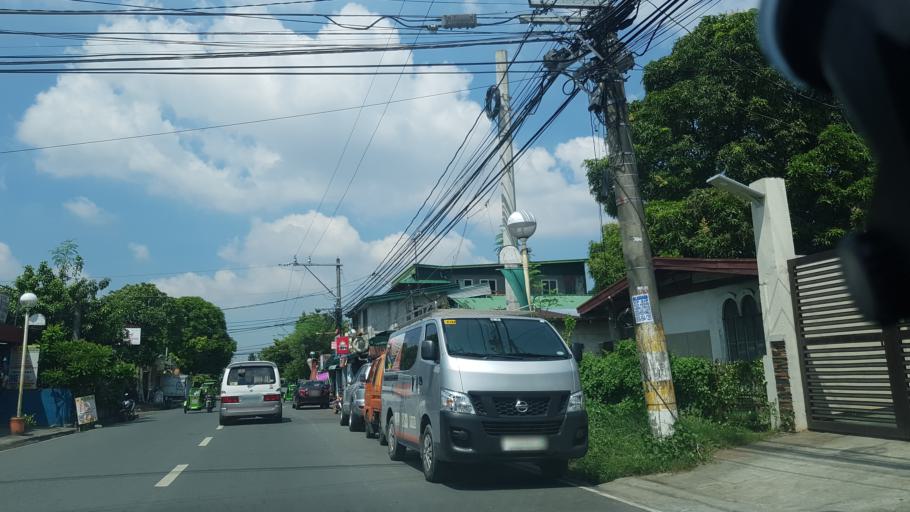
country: PH
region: Calabarzon
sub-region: Province of Rizal
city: Las Pinas
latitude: 14.4268
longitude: 120.9971
